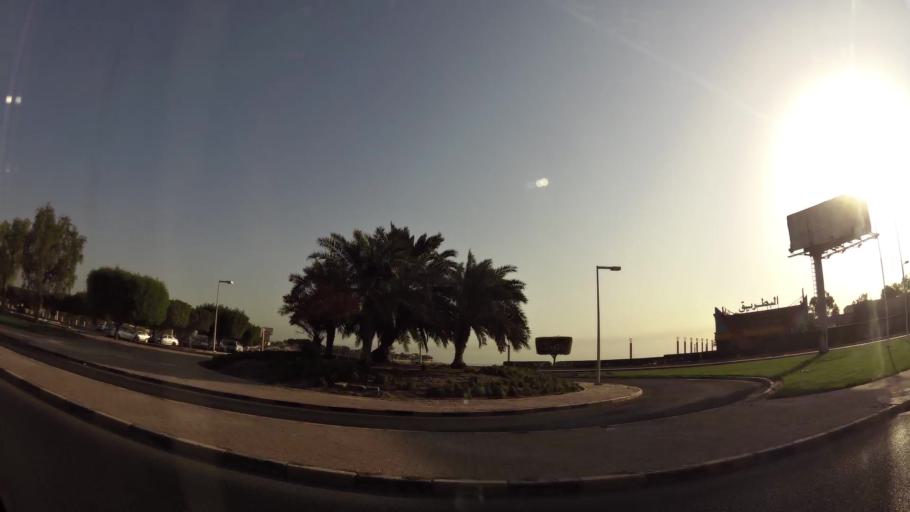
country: KW
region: Al Asimah
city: Ad Dasmah
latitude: 29.3607
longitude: 48.0244
